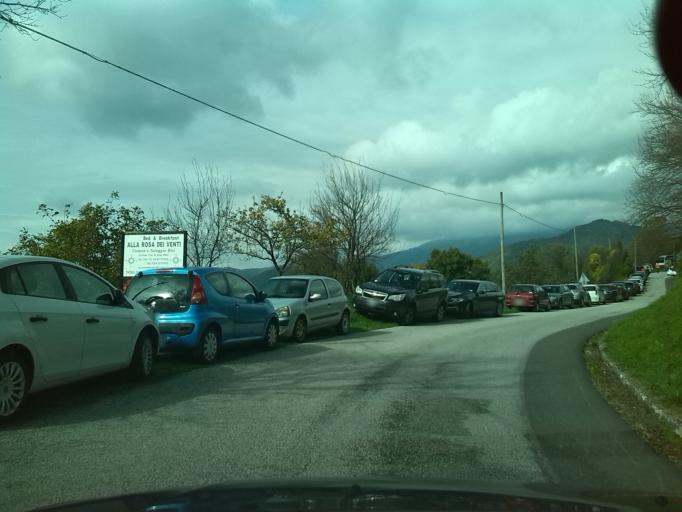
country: IT
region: Friuli Venezia Giulia
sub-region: Provincia di Udine
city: Clodig
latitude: 46.1420
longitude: 13.6161
